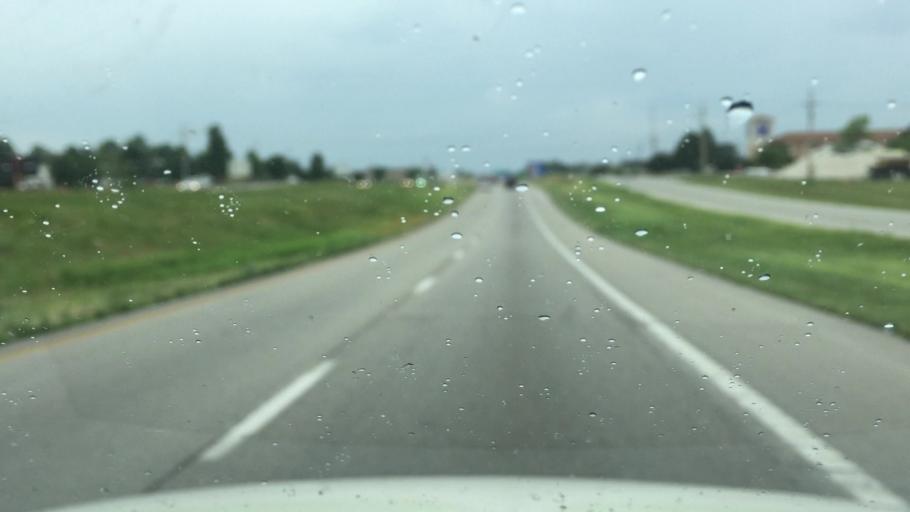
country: US
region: Missouri
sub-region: Jackson County
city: Lees Summit
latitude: 38.9027
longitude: -94.3515
